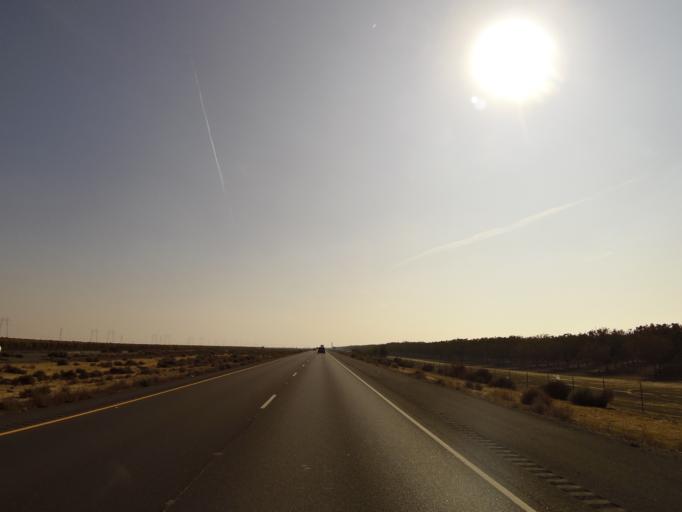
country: US
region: California
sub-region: Kings County
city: Kettleman City
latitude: 35.9146
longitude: -119.8919
